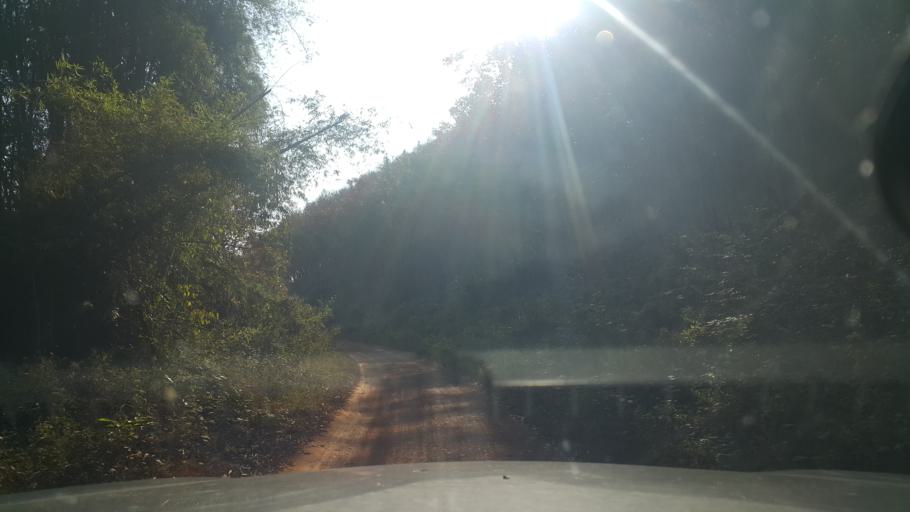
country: TH
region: Loei
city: Chiang Khan
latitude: 17.8285
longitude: 101.6112
